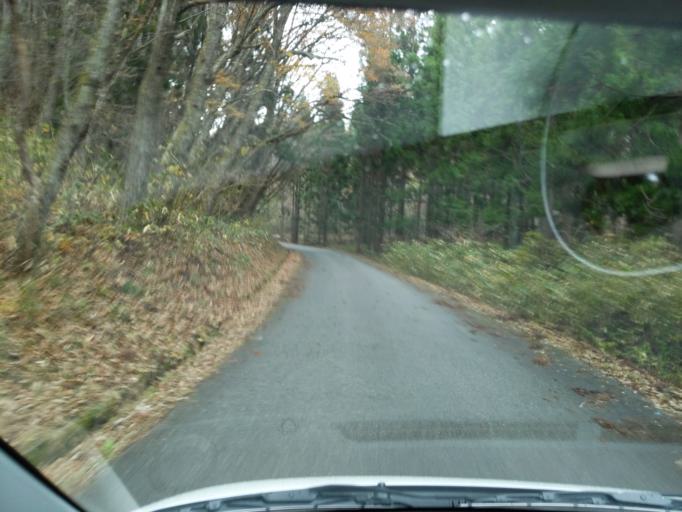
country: JP
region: Iwate
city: Ichinoseki
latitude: 38.9757
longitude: 141.0002
